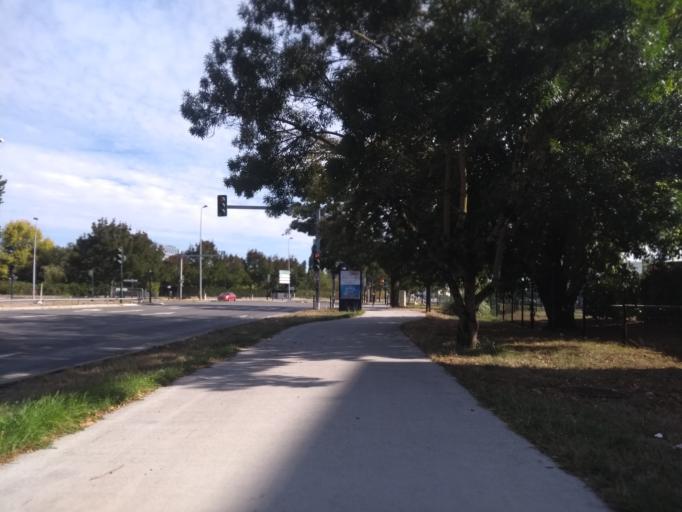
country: FR
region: Aquitaine
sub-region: Departement de la Gironde
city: Le Bouscat
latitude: 44.8903
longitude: -0.5623
